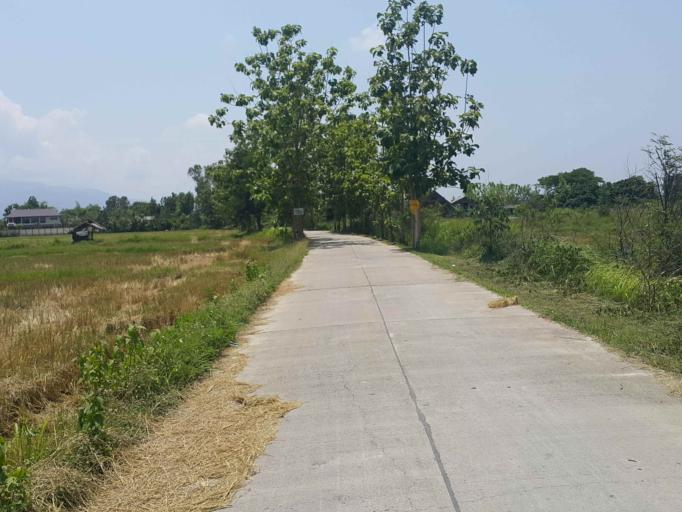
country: TH
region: Chiang Mai
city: San Sai
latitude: 18.8148
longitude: 99.0671
